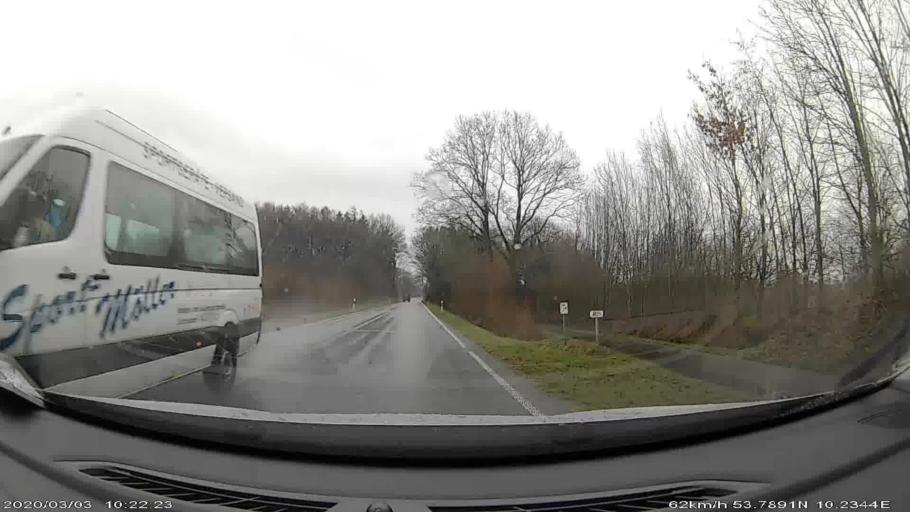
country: DE
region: Schleswig-Holstein
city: Sulfeld
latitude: 53.7862
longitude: 10.2382
